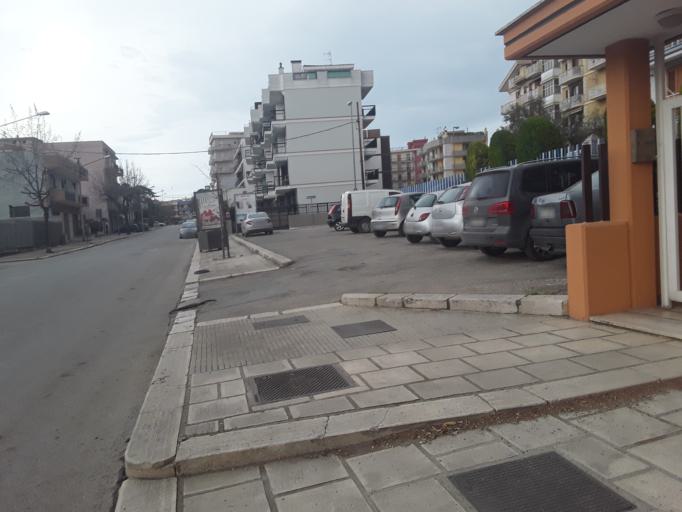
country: IT
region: Apulia
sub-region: Provincia di Bari
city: Ruvo di Puglia
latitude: 41.1176
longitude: 16.4773
